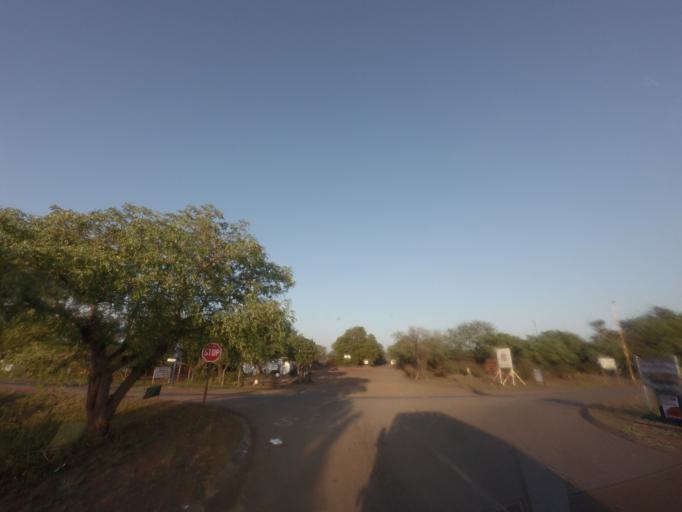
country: ZA
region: Mpumalanga
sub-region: Ehlanzeni District
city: Komatipoort
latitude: -25.4410
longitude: 31.9621
